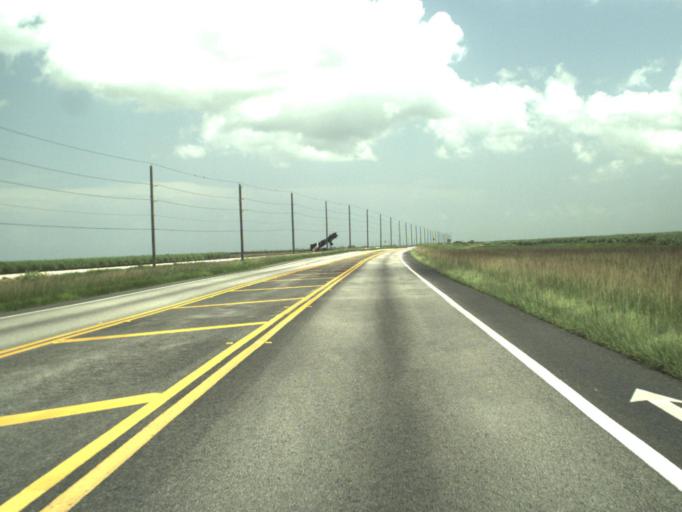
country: US
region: Florida
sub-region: Palm Beach County
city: Belle Glade
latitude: 26.7361
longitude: -80.6634
